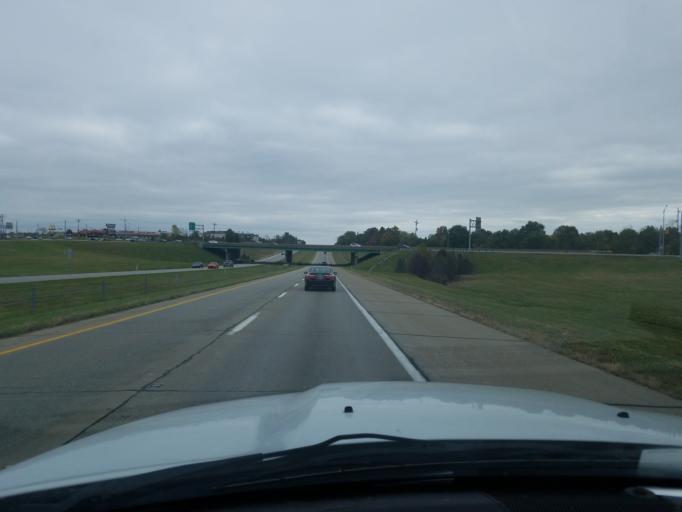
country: US
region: Indiana
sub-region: Floyd County
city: New Albany
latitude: 38.3352
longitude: -85.8199
